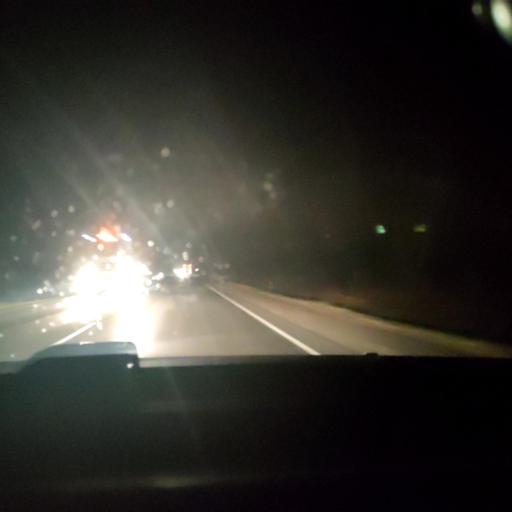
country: RU
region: Voronezj
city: Latnaya
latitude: 51.6372
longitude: 38.6799
